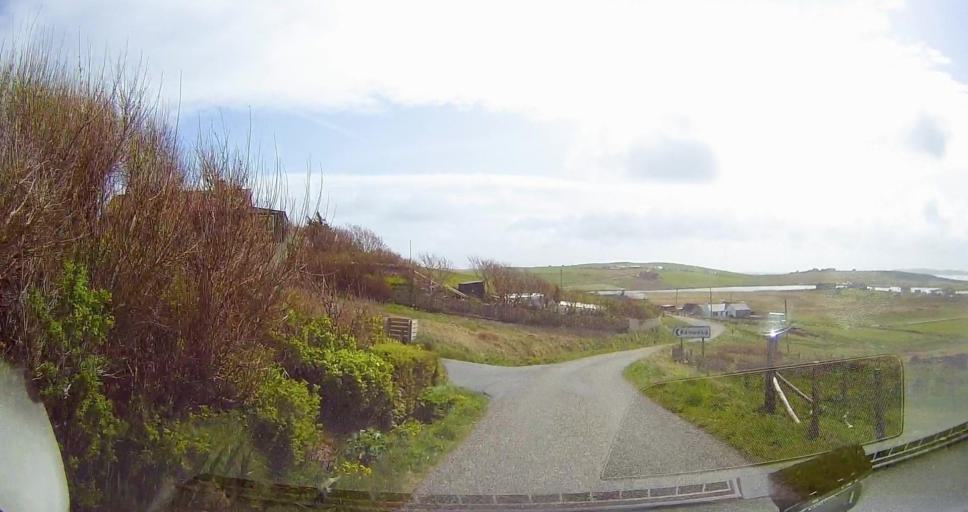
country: GB
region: Scotland
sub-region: Shetland Islands
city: Sandwick
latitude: 60.0491
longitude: -1.2181
